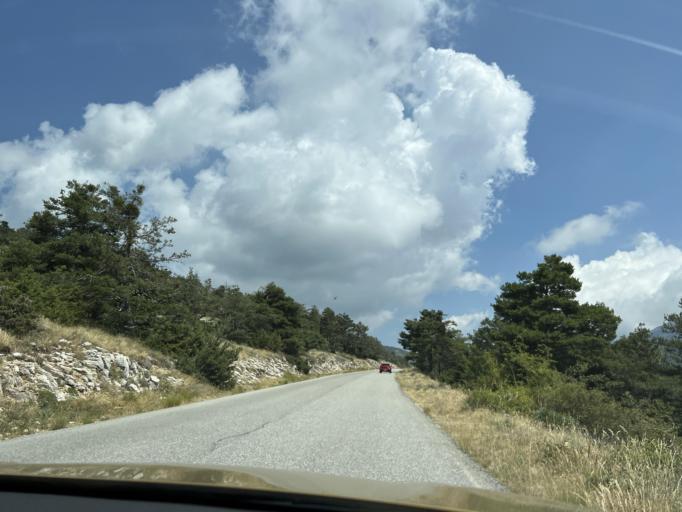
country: FR
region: Provence-Alpes-Cote d'Azur
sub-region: Departement des Alpes-Maritimes
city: Puget-Theniers
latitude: 43.8290
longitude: 6.9191
